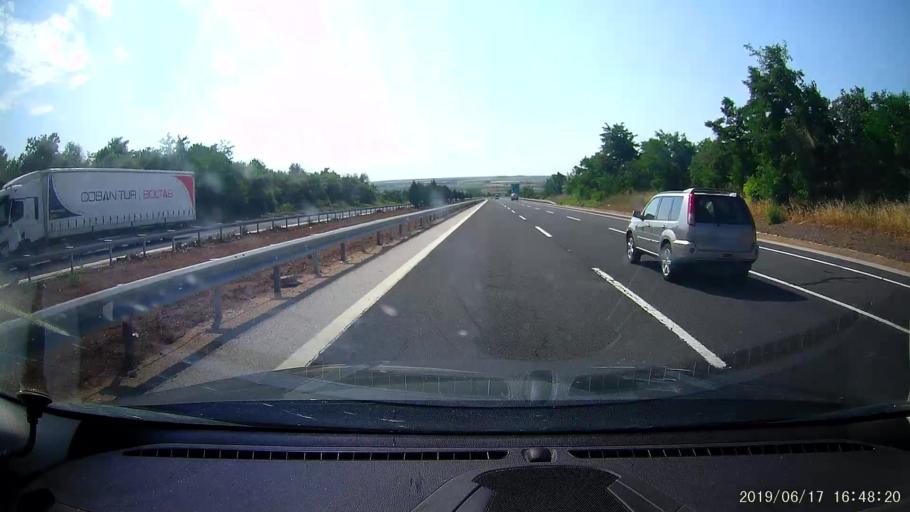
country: TR
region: Kirklareli
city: Babaeski
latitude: 41.5053
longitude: 27.1451
